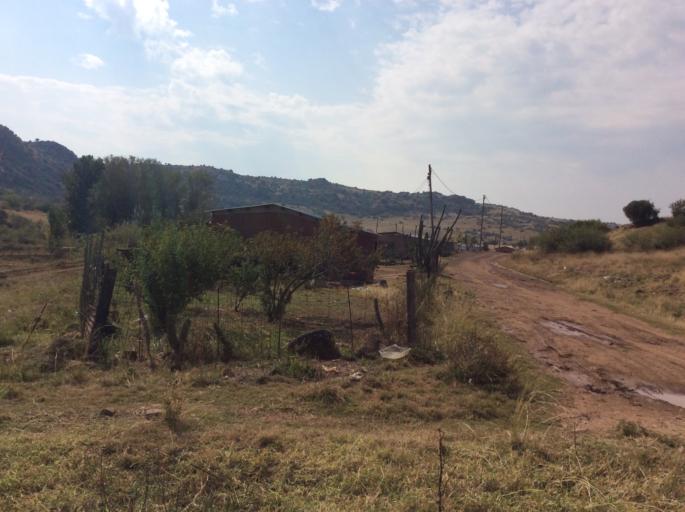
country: LS
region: Mafeteng
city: Mafeteng
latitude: -29.9824
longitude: 27.0039
